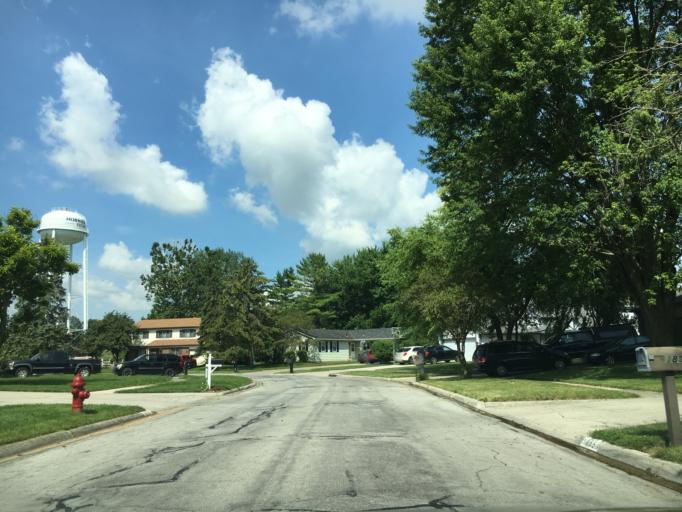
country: US
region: Ohio
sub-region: Franklin County
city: Hilliard
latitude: 39.9888
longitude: -83.1667
